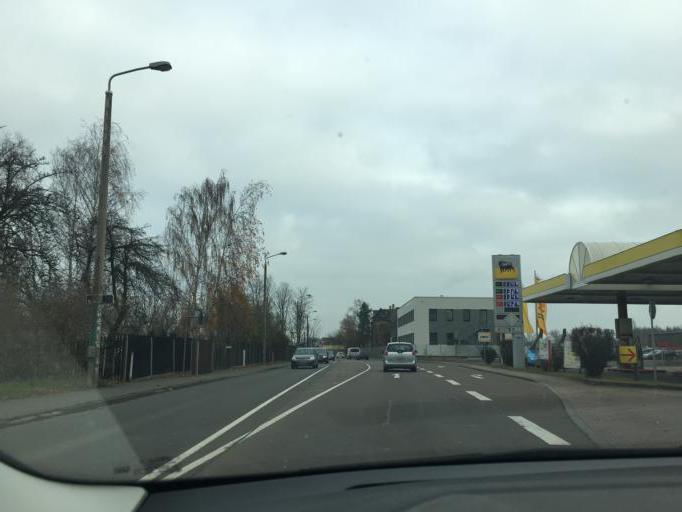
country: DE
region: Saxony
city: Taucha
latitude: 51.3385
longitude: 12.4444
